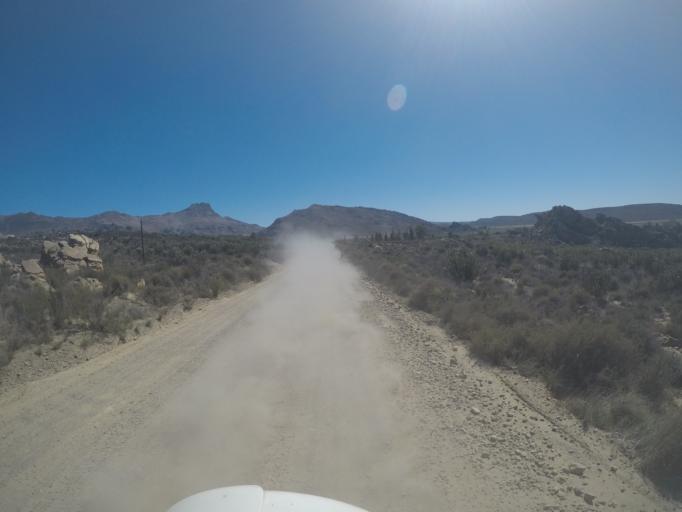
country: ZA
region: Western Cape
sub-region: Cape Winelands District Municipality
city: Ceres
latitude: -32.8729
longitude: 19.4448
